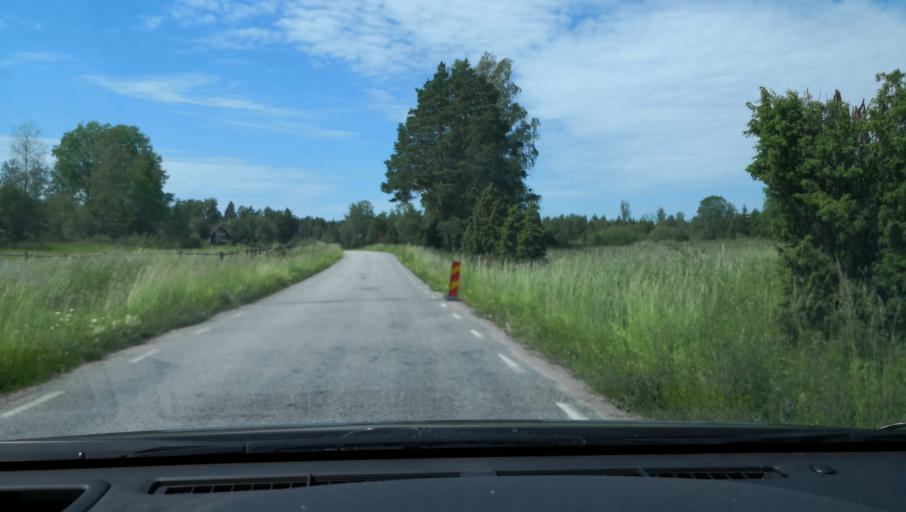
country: SE
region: Stockholm
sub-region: Sigtuna Kommun
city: Sigtuna
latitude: 59.6828
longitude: 17.6806
